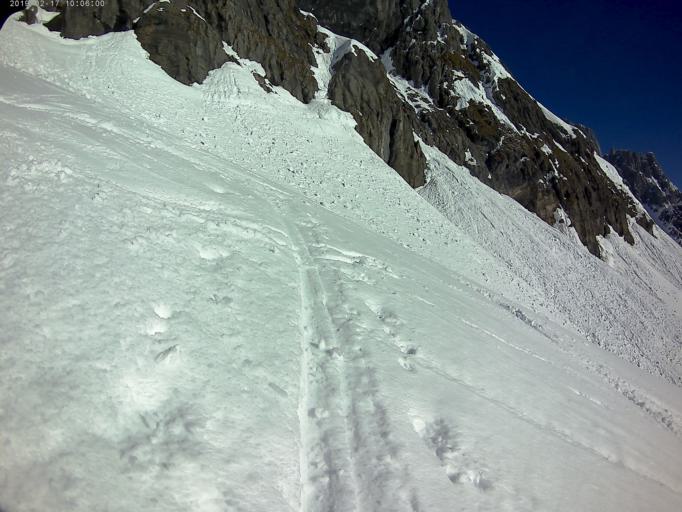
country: AT
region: Salzburg
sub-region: Politischer Bezirk Sankt Johann im Pongau
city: Muhlbach am Hochkonig
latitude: 47.4096
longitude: 13.0799
